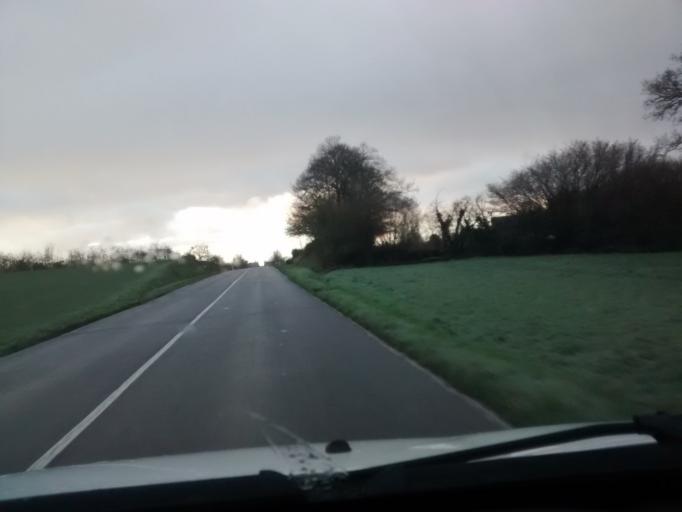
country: FR
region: Brittany
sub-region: Departement d'Ille-et-Vilaine
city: Bais
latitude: 48.0014
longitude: -1.2882
